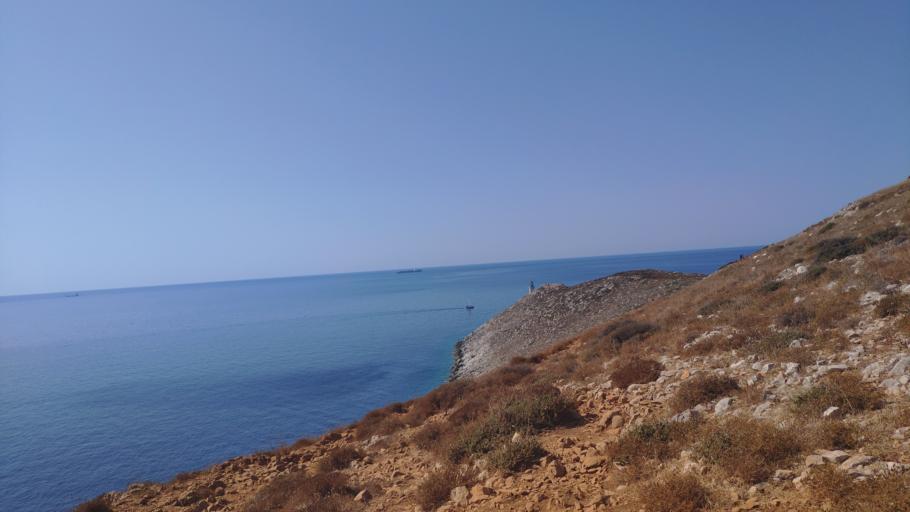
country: GR
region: Peloponnese
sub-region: Nomos Lakonias
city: Gytheio
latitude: 36.3919
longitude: 22.4838
